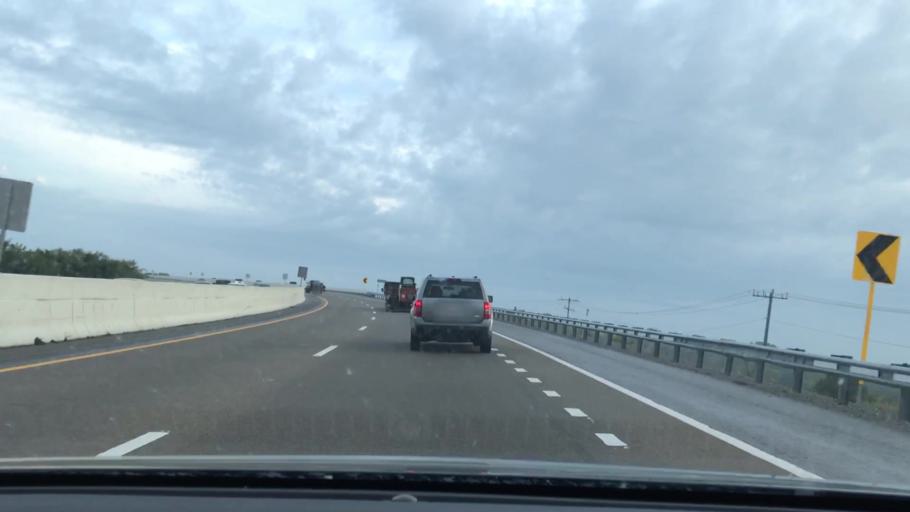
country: US
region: Tennessee
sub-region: Sumner County
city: Hendersonville
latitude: 36.3309
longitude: -86.5500
